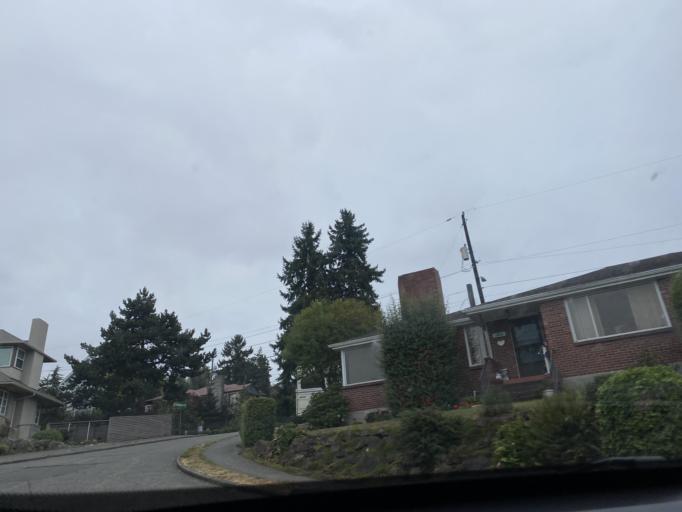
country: US
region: Washington
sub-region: King County
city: Seattle
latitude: 47.6450
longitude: -122.3727
